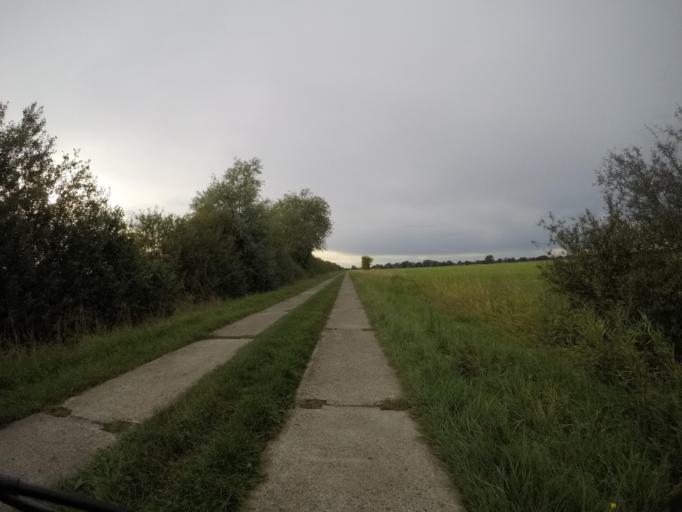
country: DE
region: Lower Saxony
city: Neu Darchau
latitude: 53.2702
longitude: 10.8715
